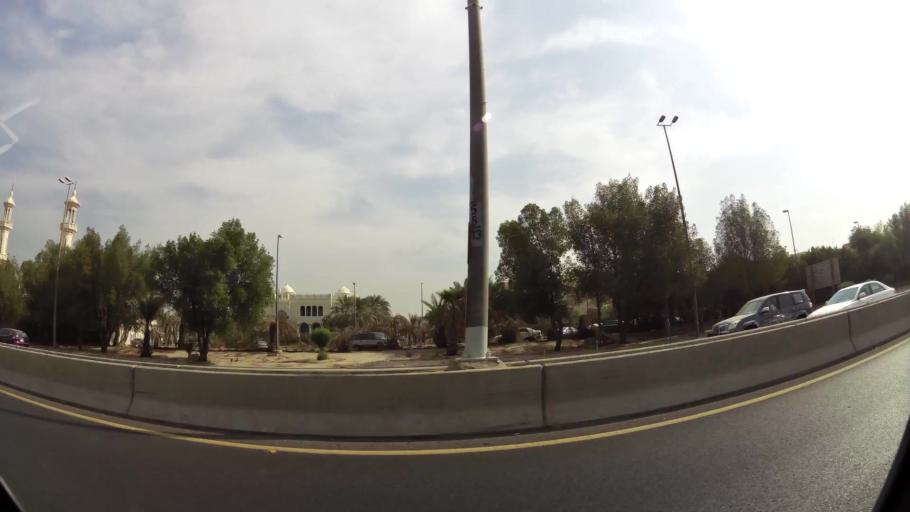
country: KW
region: Al Asimah
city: Ash Shamiyah
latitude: 29.3230
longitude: 47.9734
